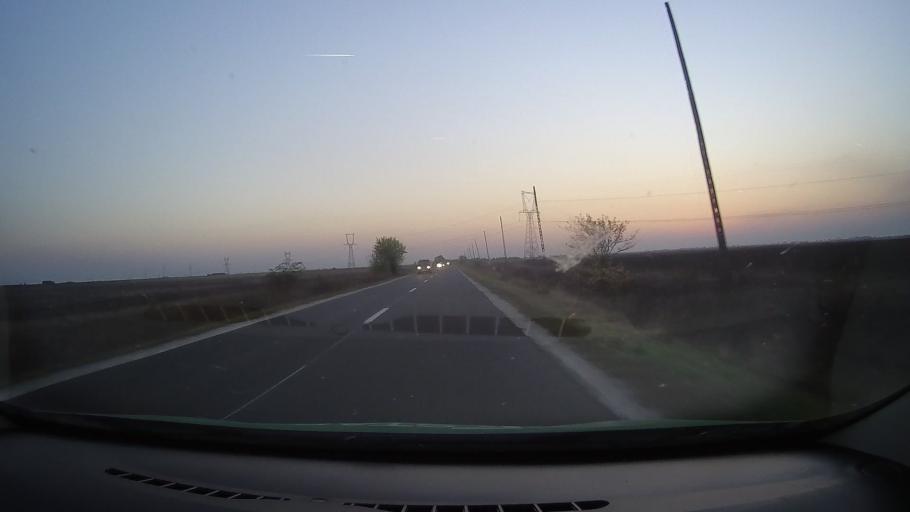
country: RO
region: Arad
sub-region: Comuna Santana
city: Santana
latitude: 46.3190
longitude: 21.4579
